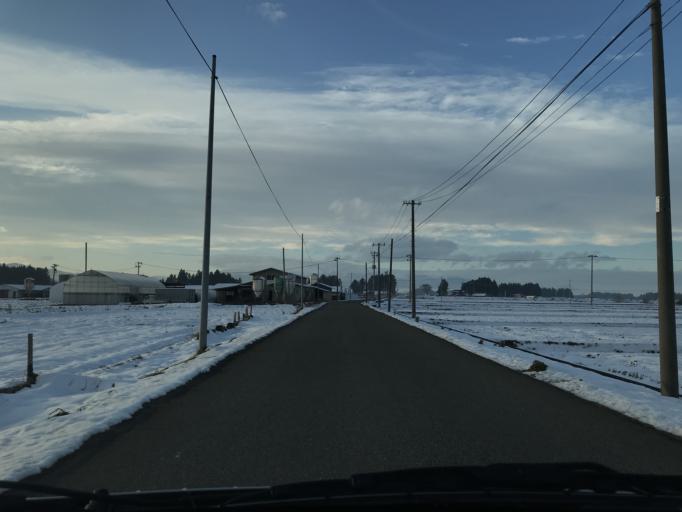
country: JP
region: Iwate
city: Mizusawa
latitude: 39.0522
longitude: 141.0987
